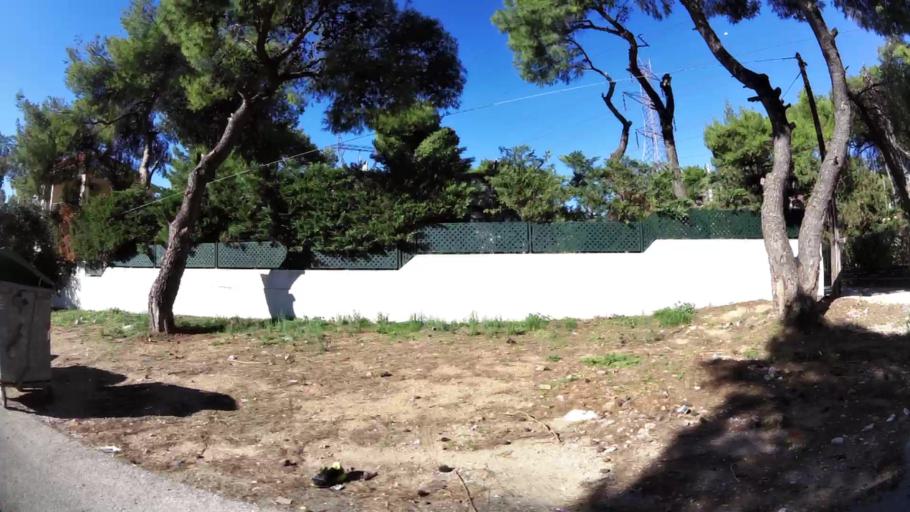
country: GR
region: Attica
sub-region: Nomarchia Anatolikis Attikis
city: Varybobi
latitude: 38.1275
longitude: 23.7891
